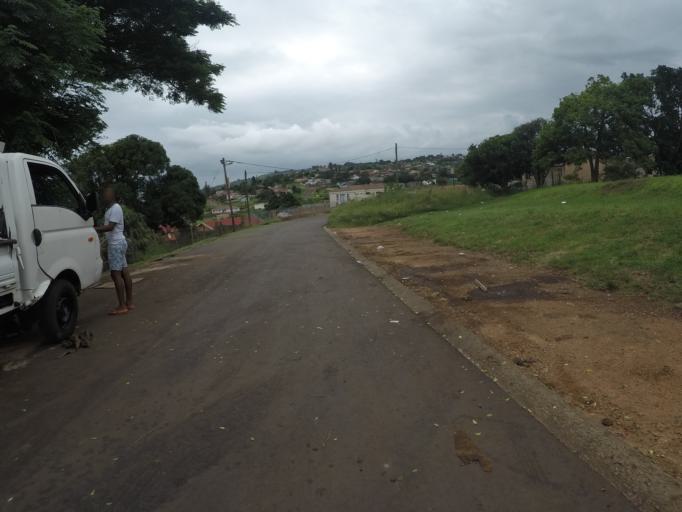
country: ZA
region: KwaZulu-Natal
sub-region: uThungulu District Municipality
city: Empangeni
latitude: -28.7773
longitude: 31.8602
